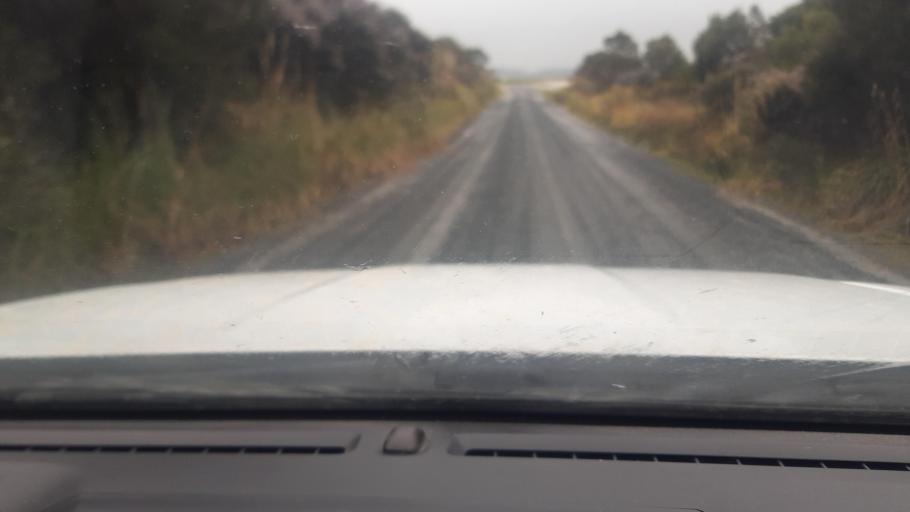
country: NZ
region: Northland
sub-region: Far North District
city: Taipa
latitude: -34.9013
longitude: 173.2777
